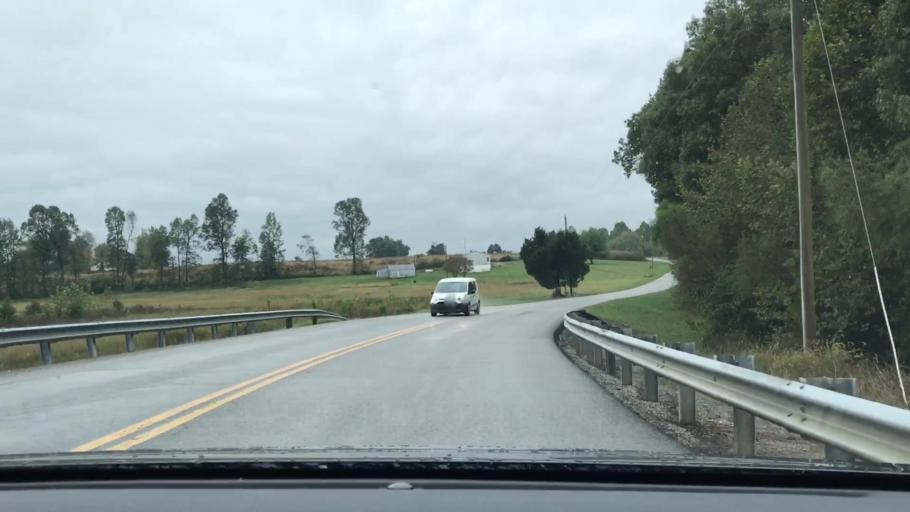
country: US
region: Kentucky
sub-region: McLean County
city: Calhoun
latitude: 37.4897
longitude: -87.2454
